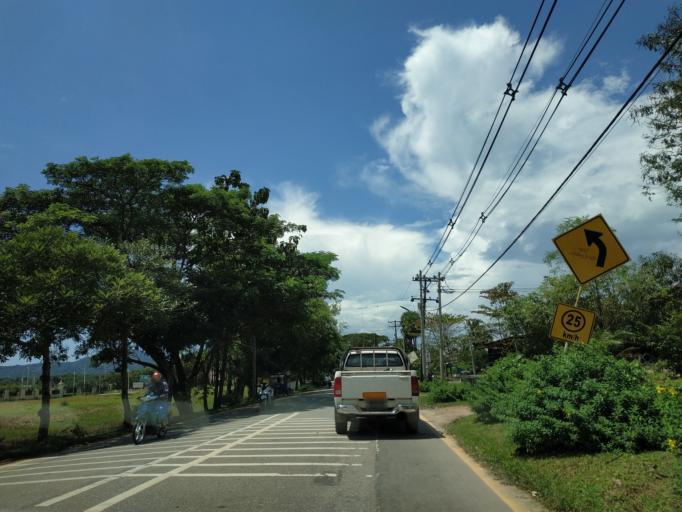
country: MM
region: Tanintharyi
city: Dawei
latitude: 14.0933
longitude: 98.1813
